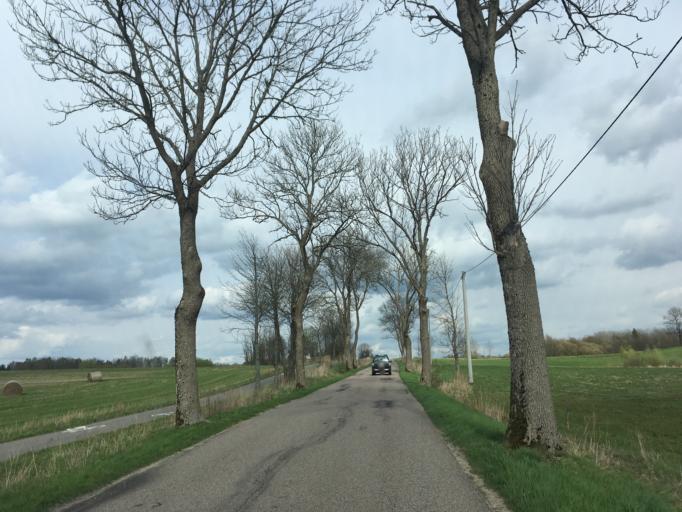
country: PL
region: Podlasie
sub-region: Powiat suwalski
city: Filipow
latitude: 54.3598
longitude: 22.7843
